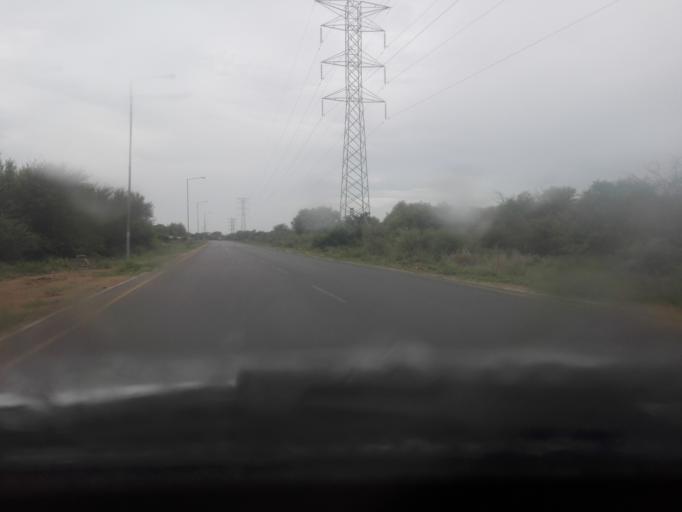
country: BW
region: South East
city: Gaborone
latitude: -24.6383
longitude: 25.8967
